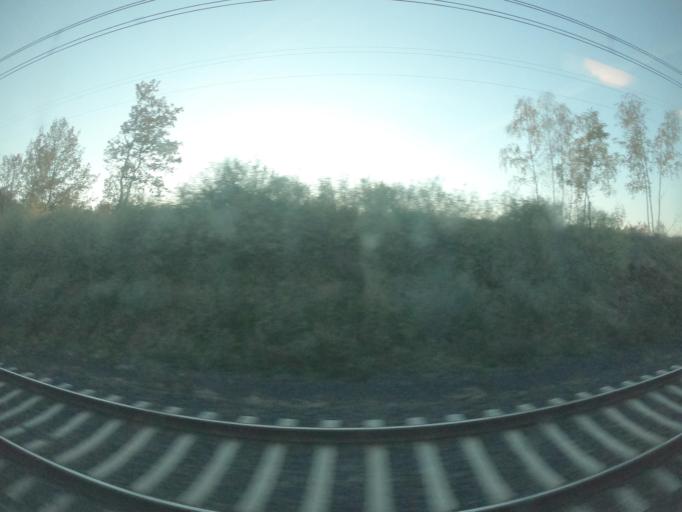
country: PL
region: West Pomeranian Voivodeship
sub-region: Powiat mysliborski
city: Boleszkowice
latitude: 52.7250
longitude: 14.5256
